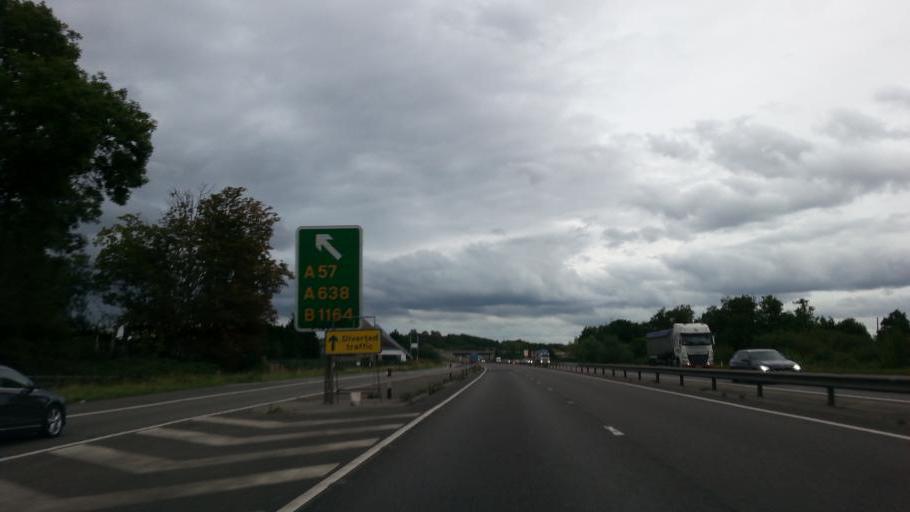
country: GB
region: England
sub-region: Nottinghamshire
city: Tuxford
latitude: 53.2575
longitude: -0.9305
